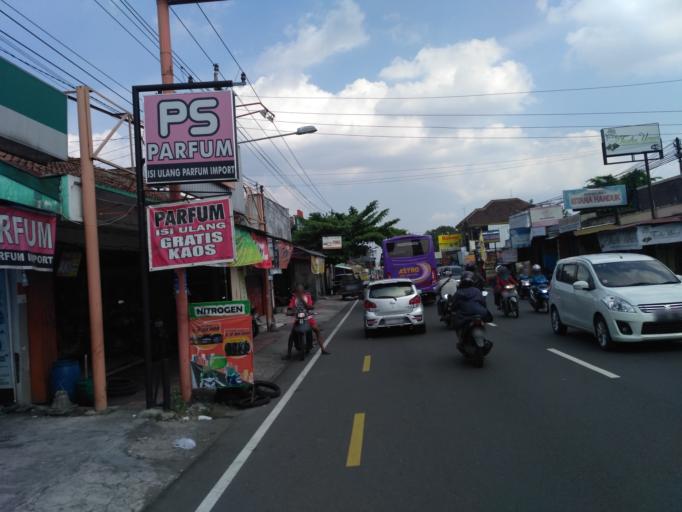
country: ID
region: Daerah Istimewa Yogyakarta
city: Melati
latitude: -7.7571
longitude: 110.3698
